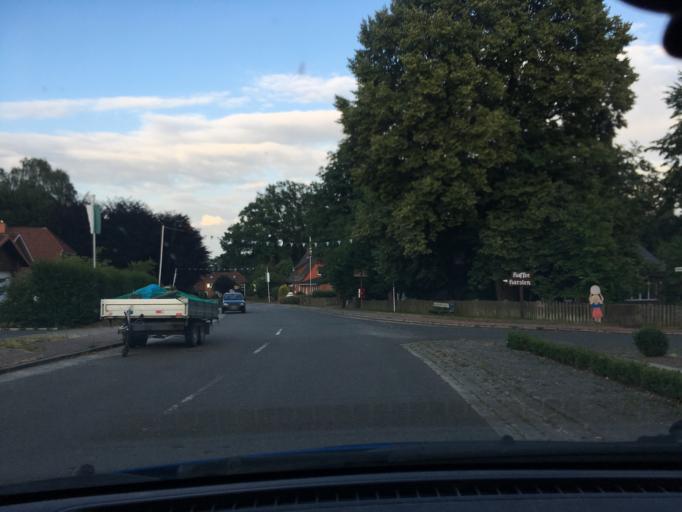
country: DE
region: Lower Saxony
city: Soderstorf
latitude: 53.1428
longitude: 10.1452
